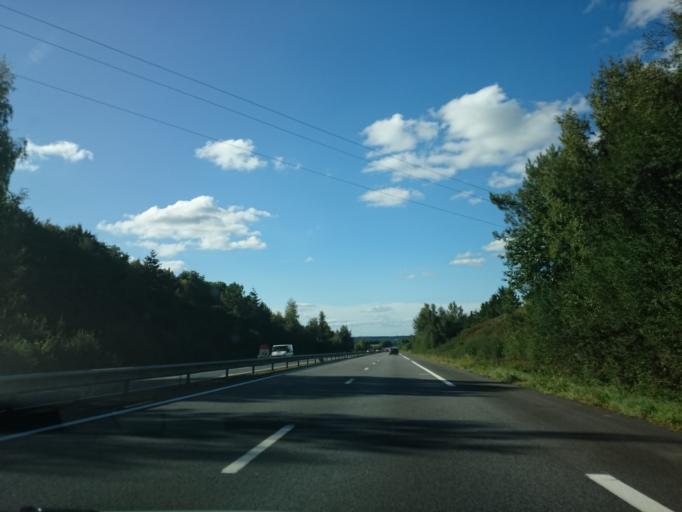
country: FR
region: Pays de la Loire
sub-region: Departement de la Loire-Atlantique
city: Derval
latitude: 47.6772
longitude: -1.6923
